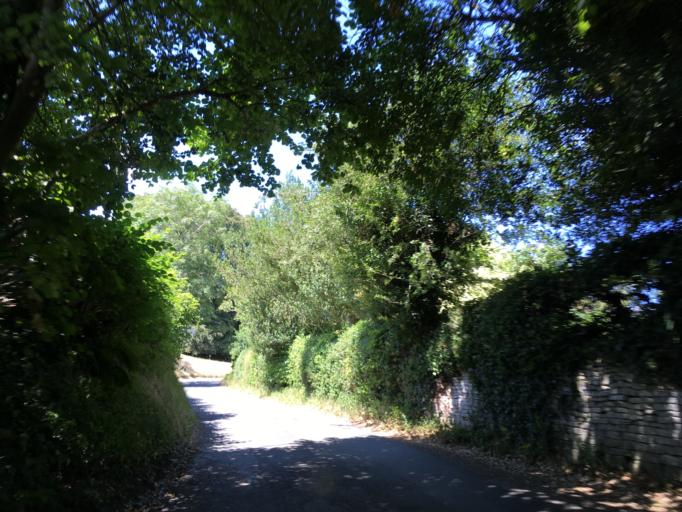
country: GB
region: England
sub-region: Gloucestershire
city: Painswick
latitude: 51.7861
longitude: -2.2201
